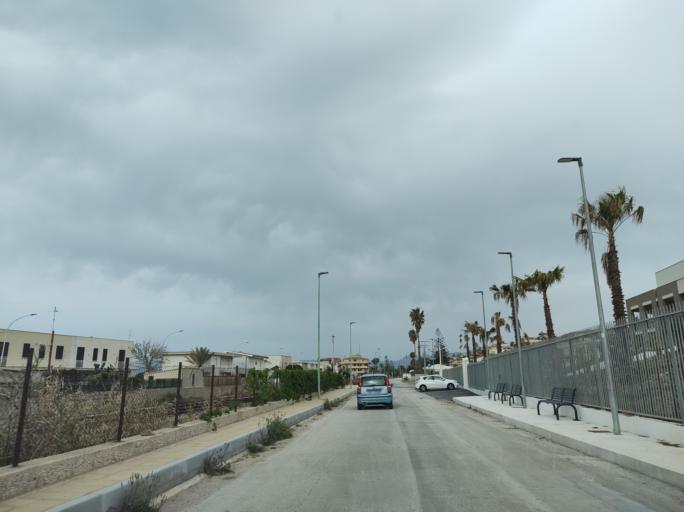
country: IT
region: Sicily
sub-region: Trapani
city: Castellammare del Golfo
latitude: 38.0247
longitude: 12.9163
